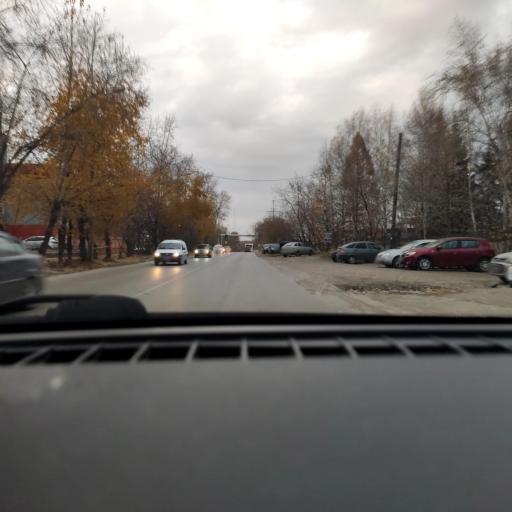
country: RU
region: Perm
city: Perm
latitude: 57.9781
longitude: 56.2689
